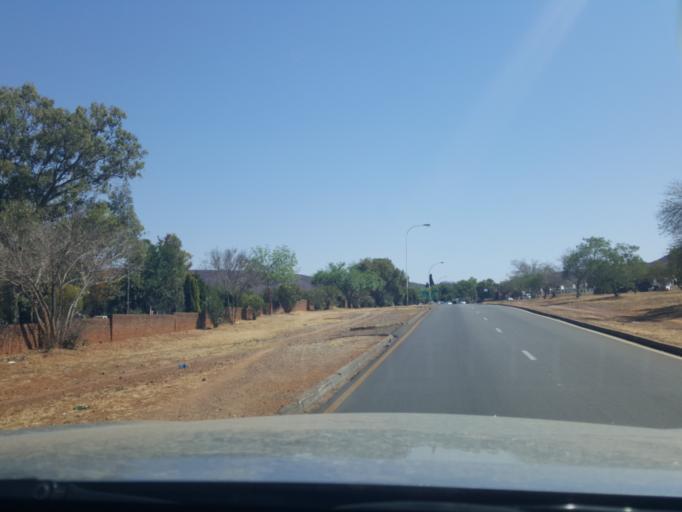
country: ZA
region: North-West
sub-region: Ngaka Modiri Molema District Municipality
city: Zeerust
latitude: -25.5391
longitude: 26.0773
